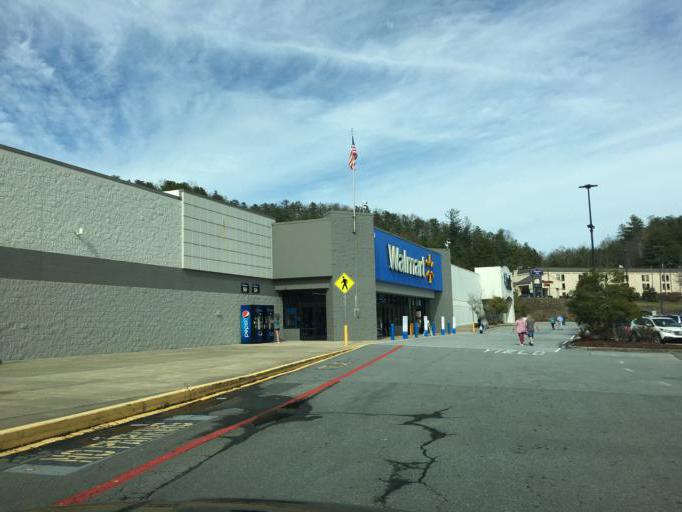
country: US
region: North Carolina
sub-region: Transylvania County
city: Brevard
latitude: 35.2770
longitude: -82.7039
